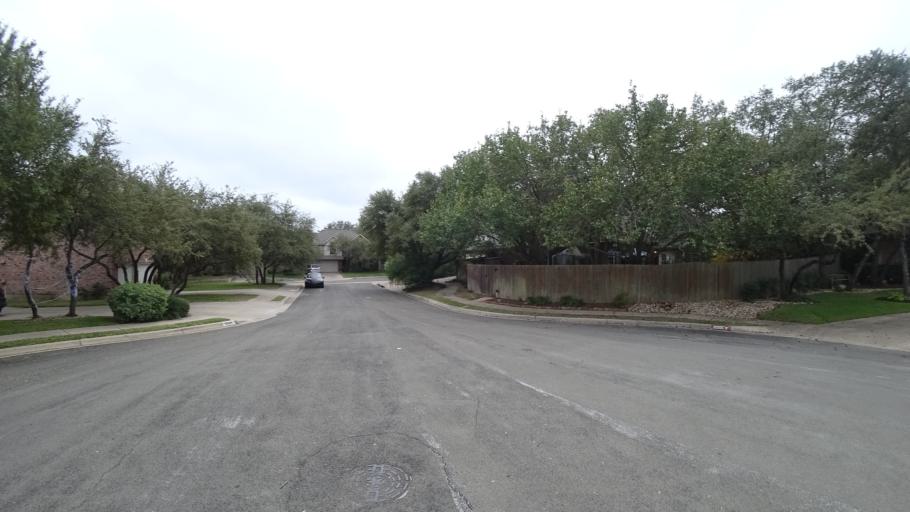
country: US
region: Texas
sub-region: Williamson County
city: Anderson Mill
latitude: 30.4389
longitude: -97.8281
